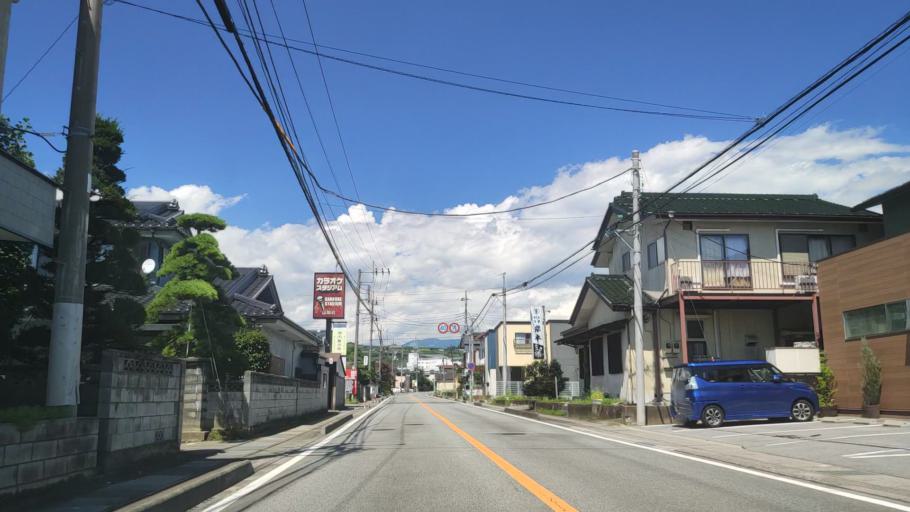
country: JP
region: Yamanashi
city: Isawa
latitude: 35.6819
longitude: 138.6618
